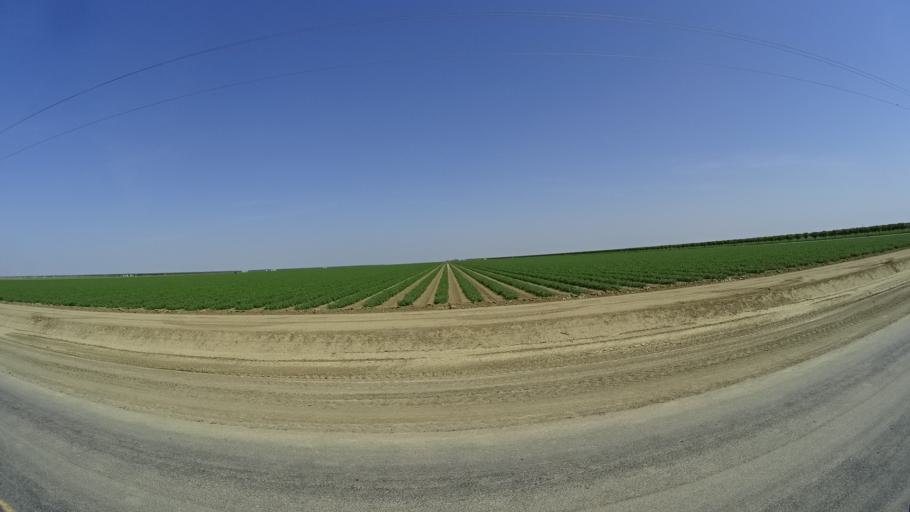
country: US
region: California
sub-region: Kings County
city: Kettleman City
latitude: 36.1377
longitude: -119.9607
